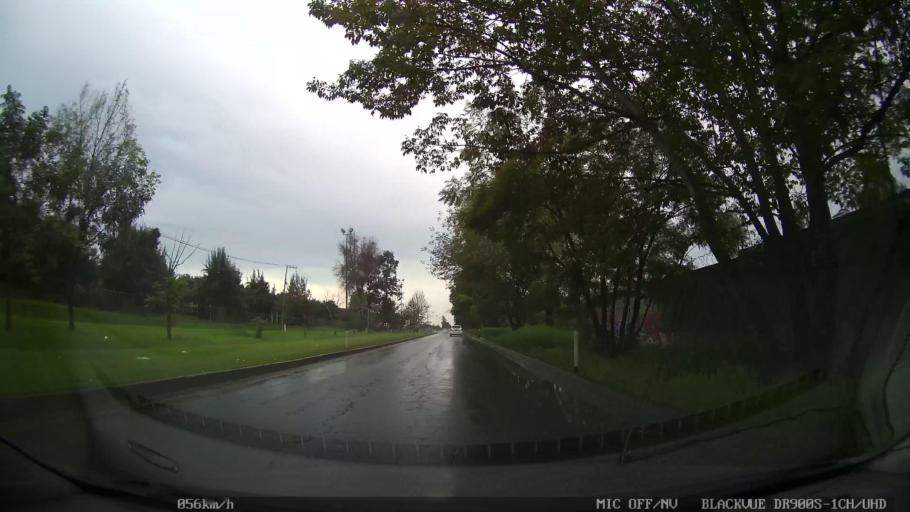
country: MX
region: Michoacan
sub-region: Uruapan
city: Santa Rosa (Santa Barbara)
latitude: 19.3946
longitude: -102.0371
